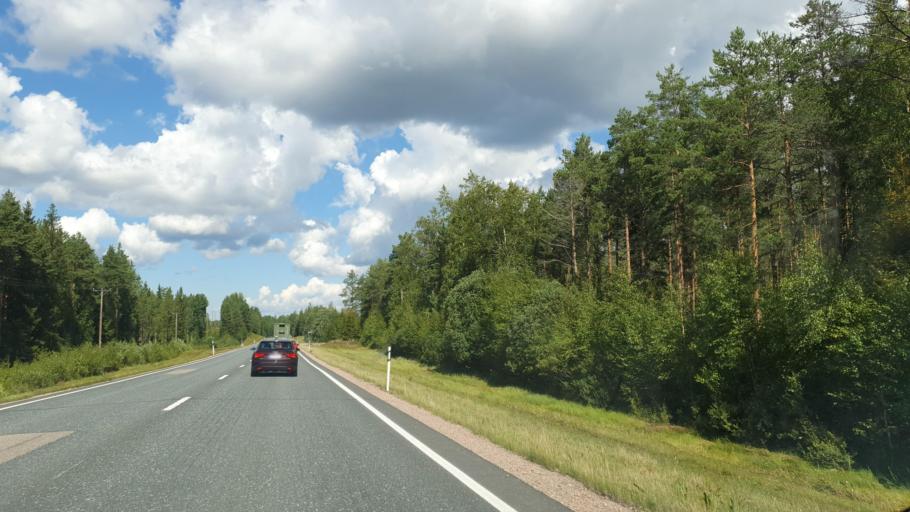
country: FI
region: Kainuu
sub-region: Kajaani
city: Kajaani
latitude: 64.1019
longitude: 27.4489
